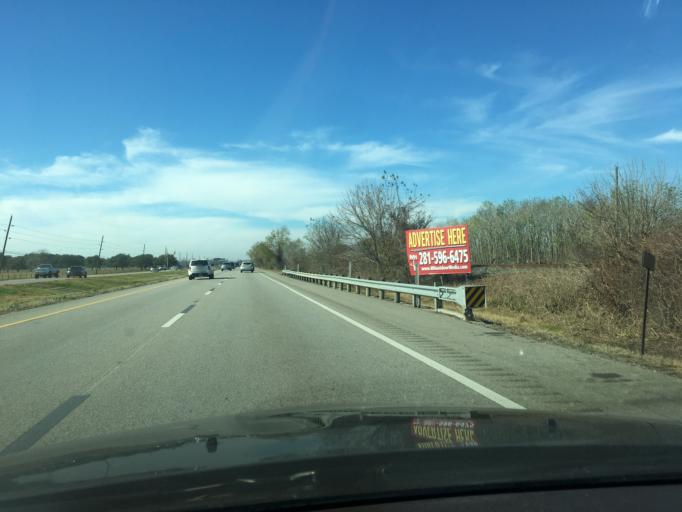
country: US
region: Texas
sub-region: Fort Bend County
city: Pecan Grove
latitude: 29.5987
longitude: -95.7160
